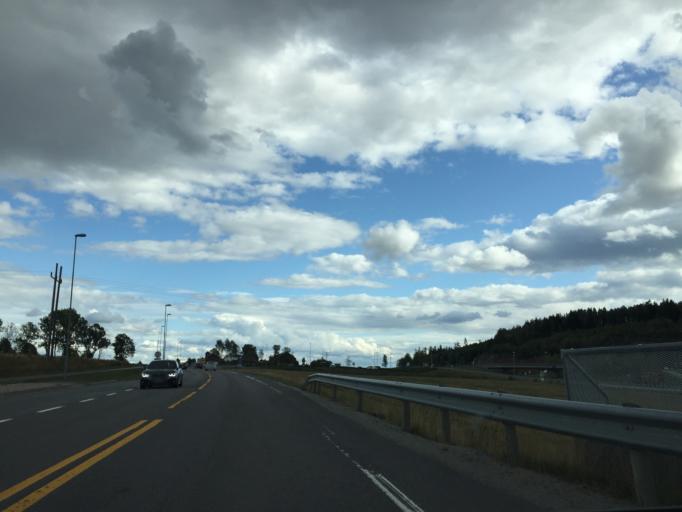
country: NO
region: Ostfold
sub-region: Spydeberg
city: Spydeberg
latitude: 59.5882
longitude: 11.1149
